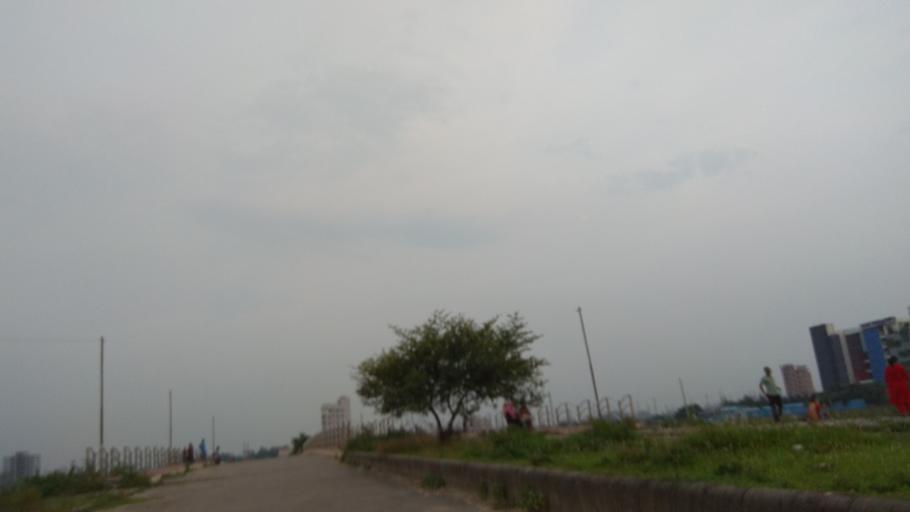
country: BD
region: Dhaka
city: Tungi
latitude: 23.8532
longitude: 90.3694
